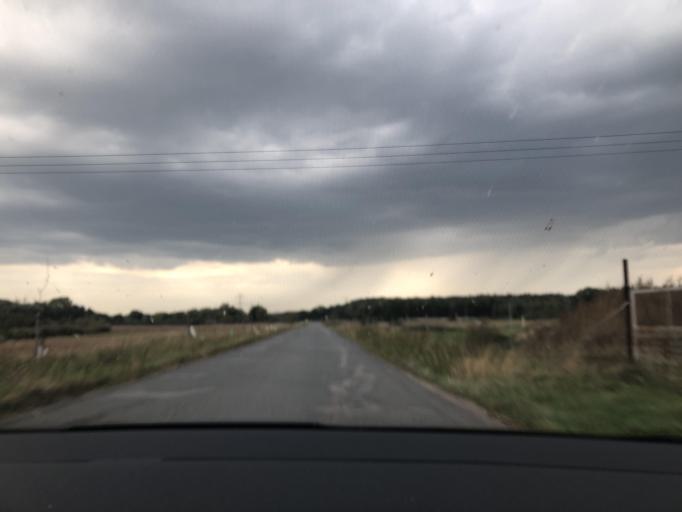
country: CZ
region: Pardubicky
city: Chvaletice
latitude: 50.0512
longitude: 15.4039
